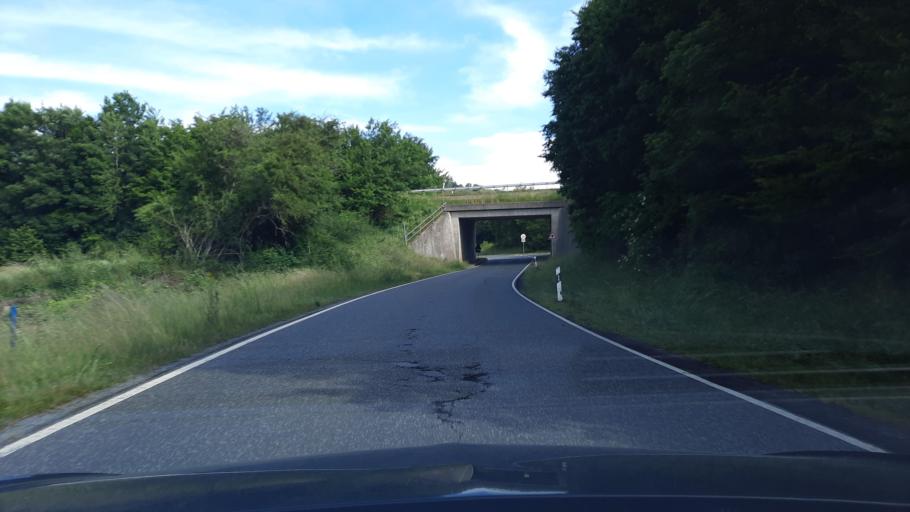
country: DE
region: Rheinland-Pfalz
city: Volkesfeld
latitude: 50.4181
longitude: 7.1651
